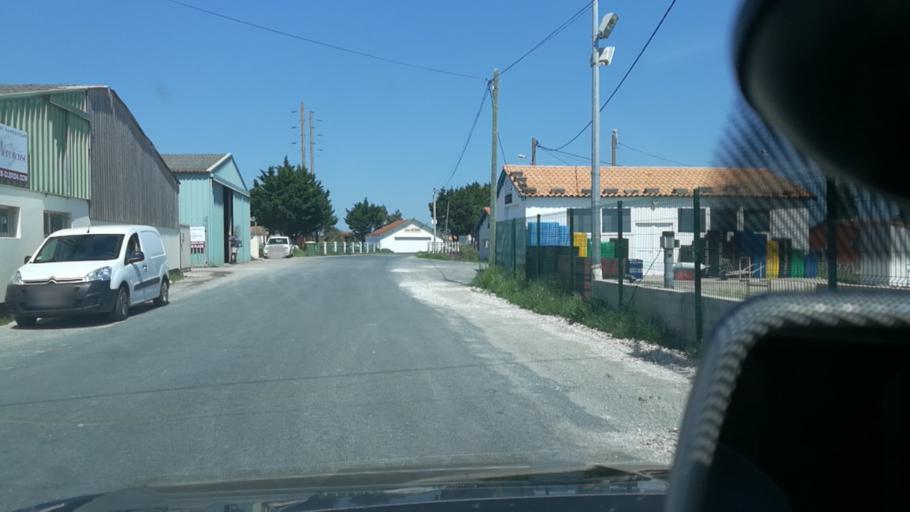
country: FR
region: Poitou-Charentes
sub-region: Departement de la Charente-Maritime
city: Saint-Trojan-les-Bains
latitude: 45.8700
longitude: -1.2191
